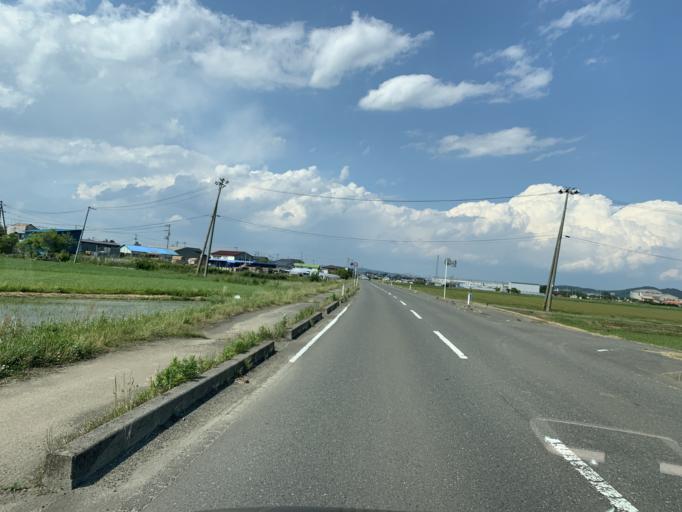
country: JP
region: Miyagi
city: Wakuya
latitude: 38.4644
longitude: 141.1283
